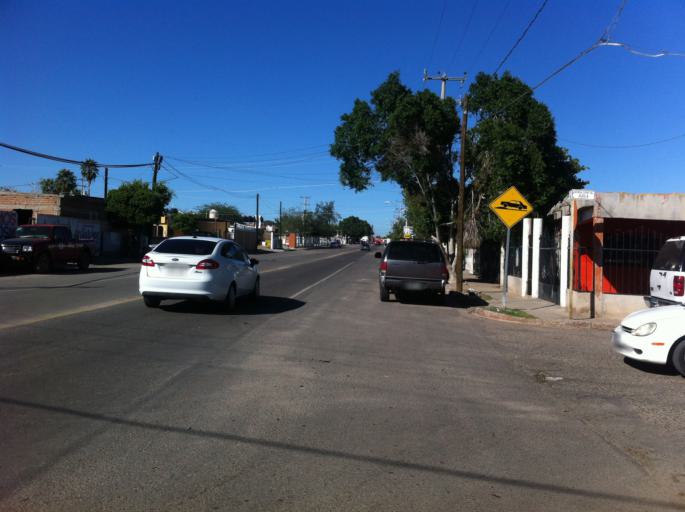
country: MX
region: Sonora
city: Hermosillo
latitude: 29.0998
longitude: -111.0049
